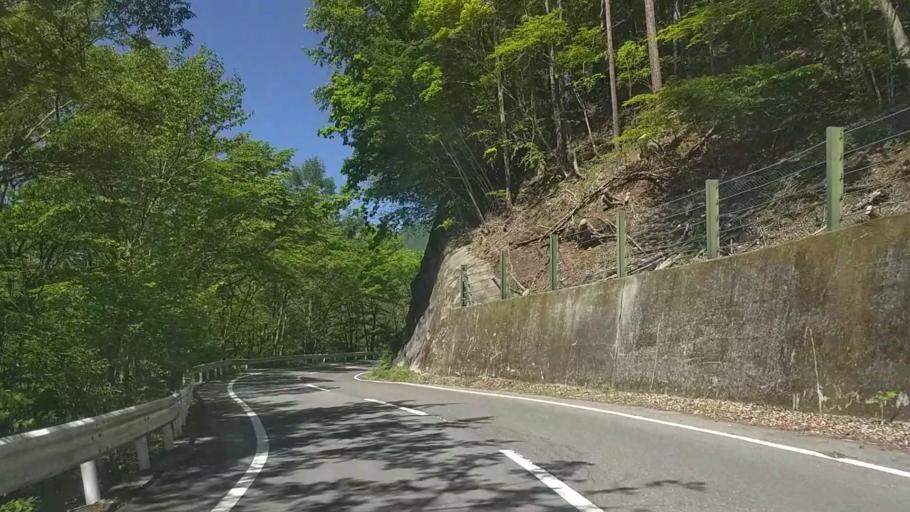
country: JP
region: Yamanashi
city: Nirasaki
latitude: 35.8804
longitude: 138.4551
